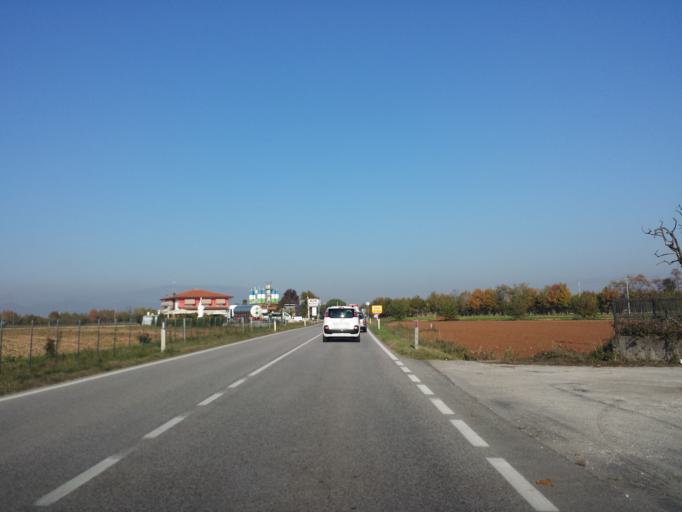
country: IT
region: Veneto
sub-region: Provincia di Treviso
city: Valla
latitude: 45.7245
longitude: 11.9529
